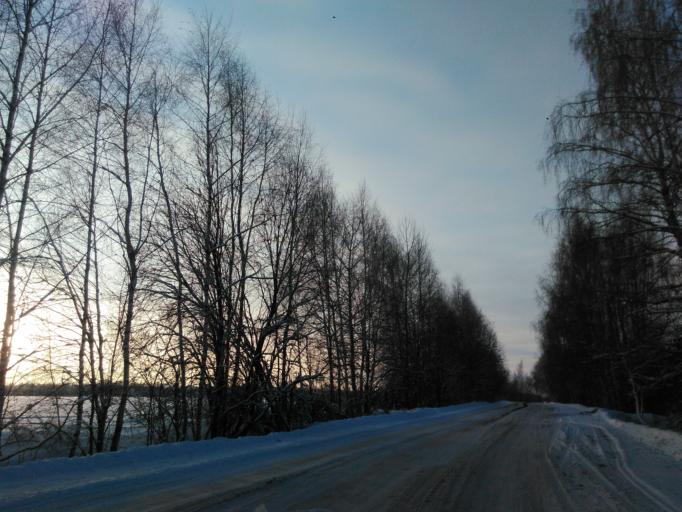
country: RU
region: Tverskaya
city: Zavidovo
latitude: 56.6405
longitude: 36.6309
